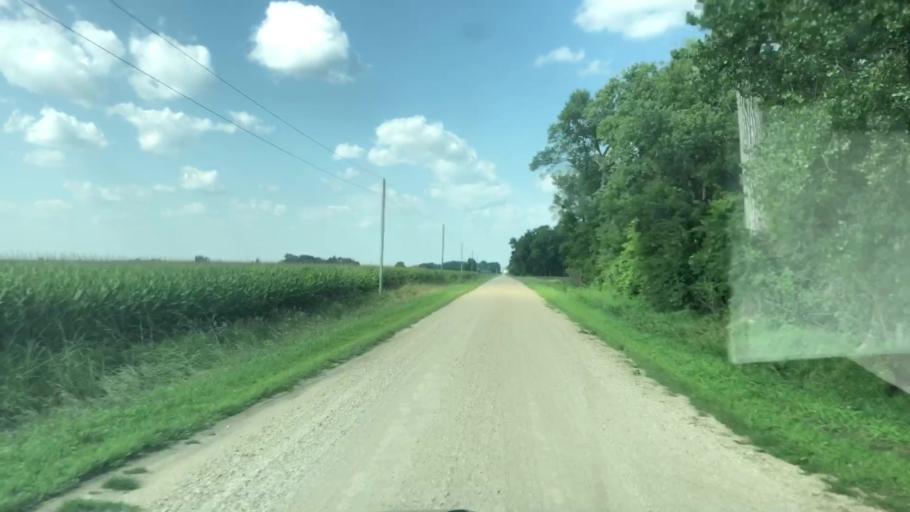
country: US
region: Iowa
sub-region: O'Brien County
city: Sheldon
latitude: 43.1629
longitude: -95.7822
